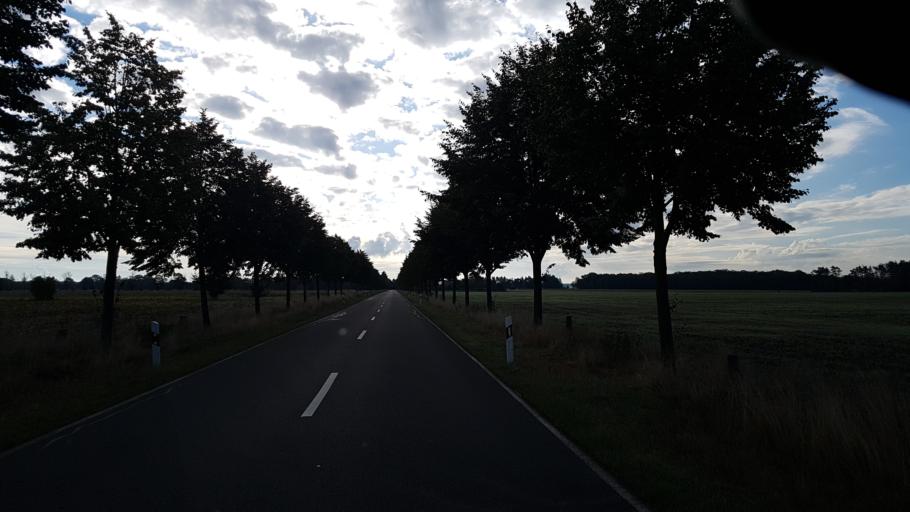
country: DE
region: Brandenburg
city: Welzow
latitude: 51.5536
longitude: 14.1735
